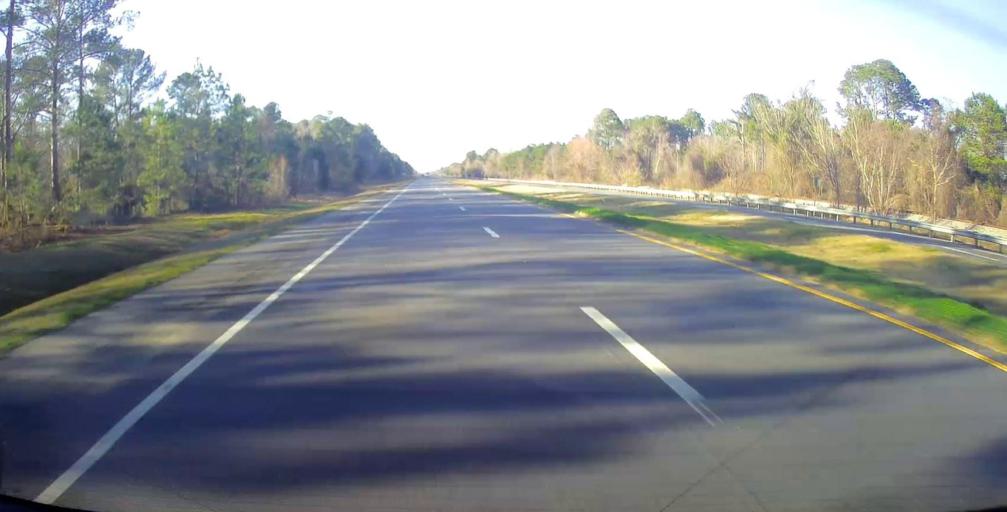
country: US
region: Georgia
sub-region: Lee County
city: Leesburg
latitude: 31.8276
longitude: -84.2175
